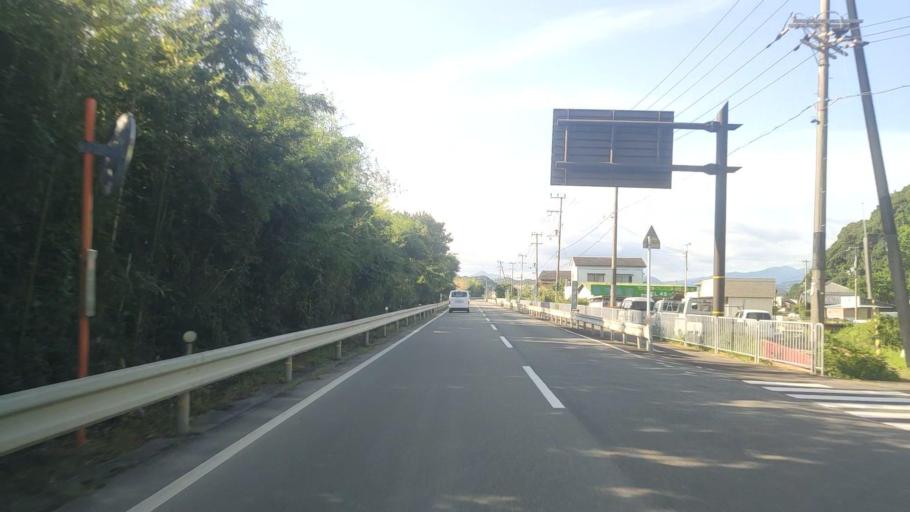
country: JP
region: Wakayama
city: Tanabe
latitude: 33.6700
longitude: 135.4080
